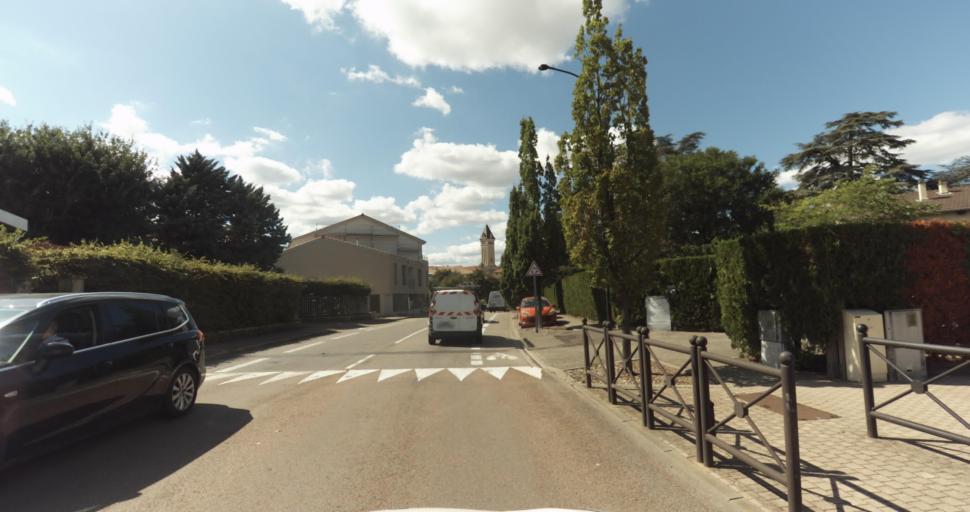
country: FR
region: Rhone-Alpes
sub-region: Departement du Rhone
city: Chaponost
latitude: 45.7083
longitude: 4.7465
